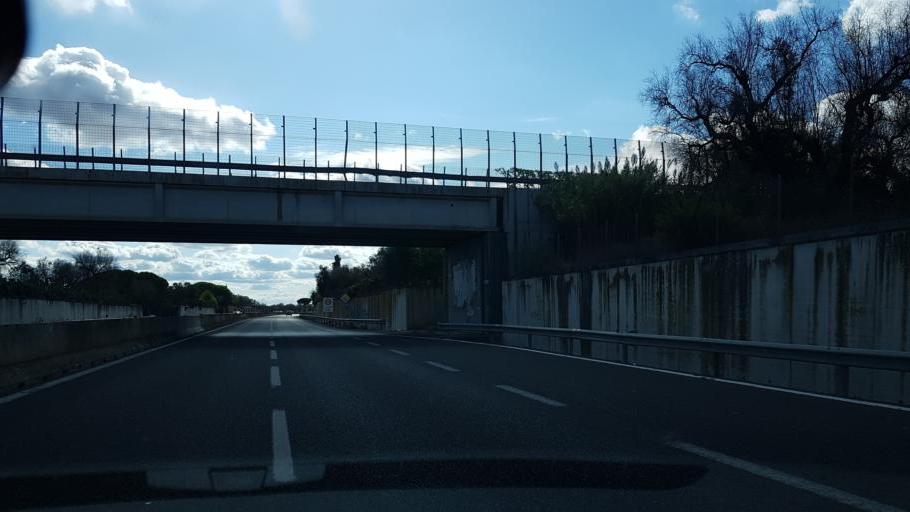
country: IT
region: Apulia
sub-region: Provincia di Brindisi
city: Torchiarolo
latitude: 40.4632
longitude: 18.0574
